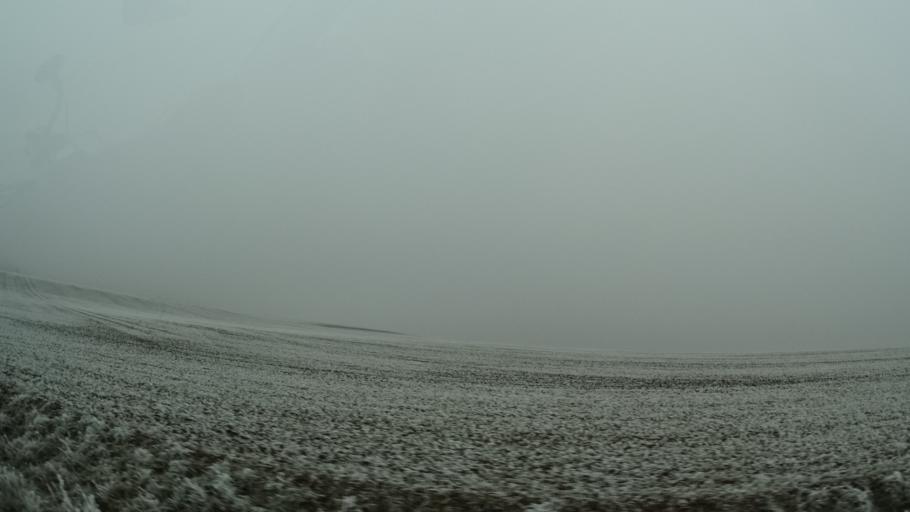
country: DE
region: Bavaria
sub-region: Regierungsbezirk Unterfranken
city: Willmars
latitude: 50.5226
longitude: 10.2996
